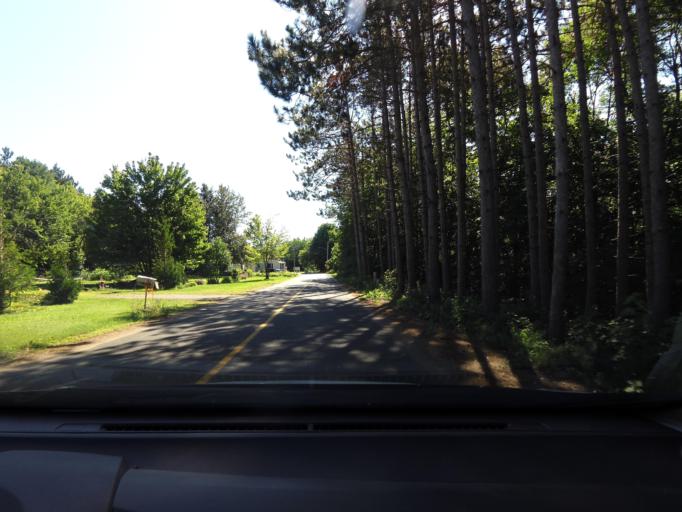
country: CA
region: Quebec
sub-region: Mauricie
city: Becancour
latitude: 46.5514
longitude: -72.4245
